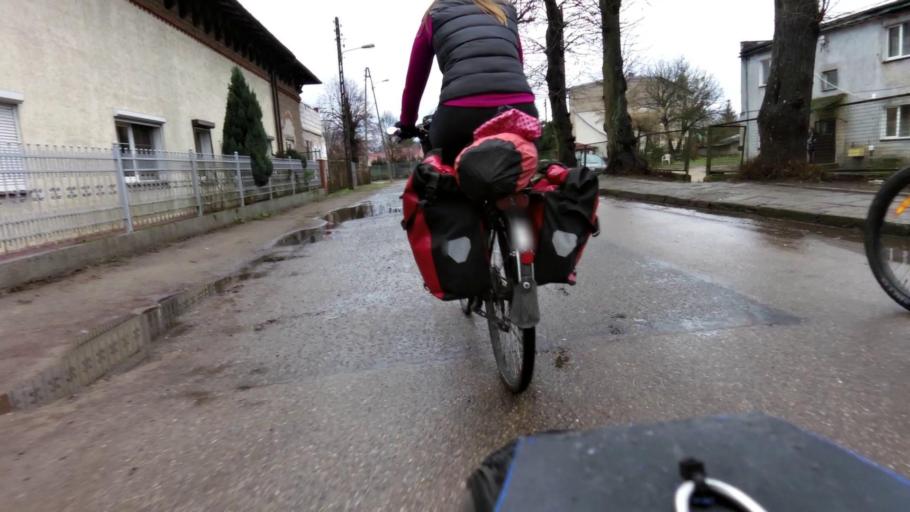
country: PL
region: Lubusz
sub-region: Powiat gorzowski
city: Witnica
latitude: 52.6842
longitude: 14.8876
